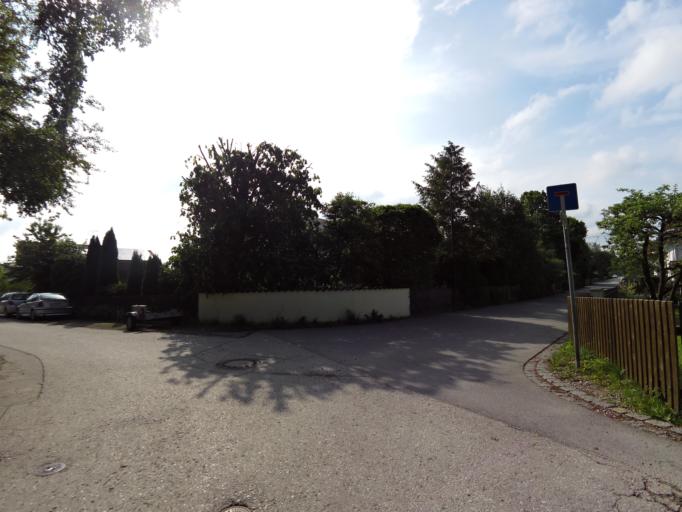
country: DE
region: Bavaria
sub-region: Upper Bavaria
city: Schaftlarn
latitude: 47.9892
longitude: 11.4526
